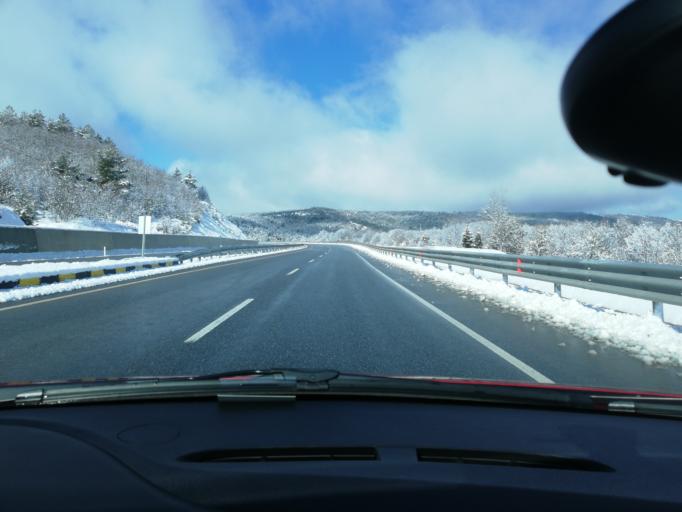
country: TR
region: Kastamonu
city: Kuzyaka
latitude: 41.3360
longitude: 33.6357
